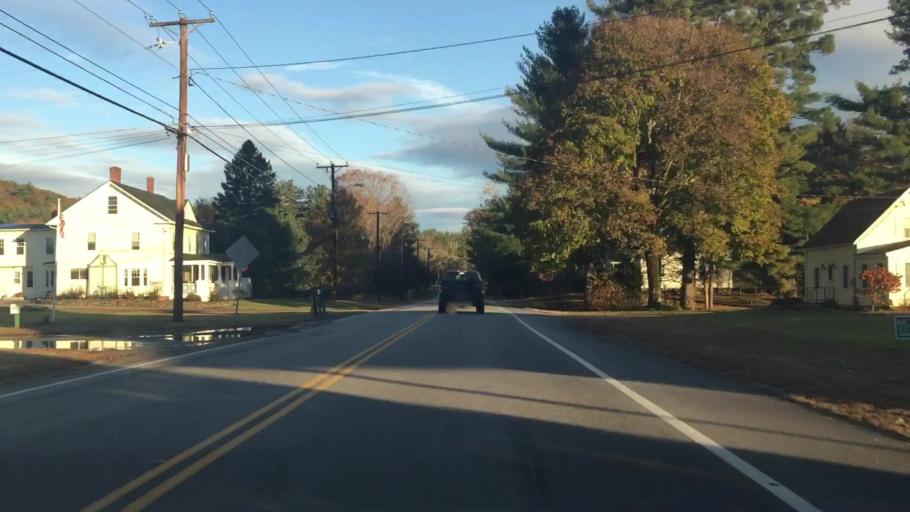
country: US
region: New Hampshire
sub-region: Cheshire County
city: Swanzey
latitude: 42.8664
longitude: -72.2812
